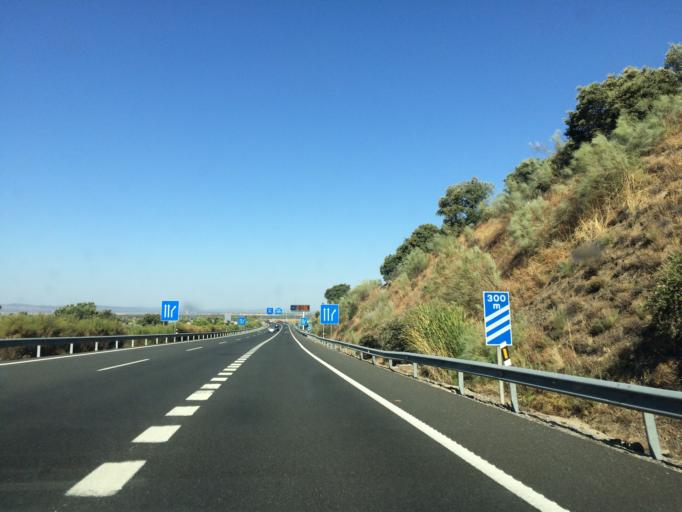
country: ES
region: Extremadura
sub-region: Provincia de Caceres
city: Millanes
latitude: 39.8717
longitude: -5.5779
